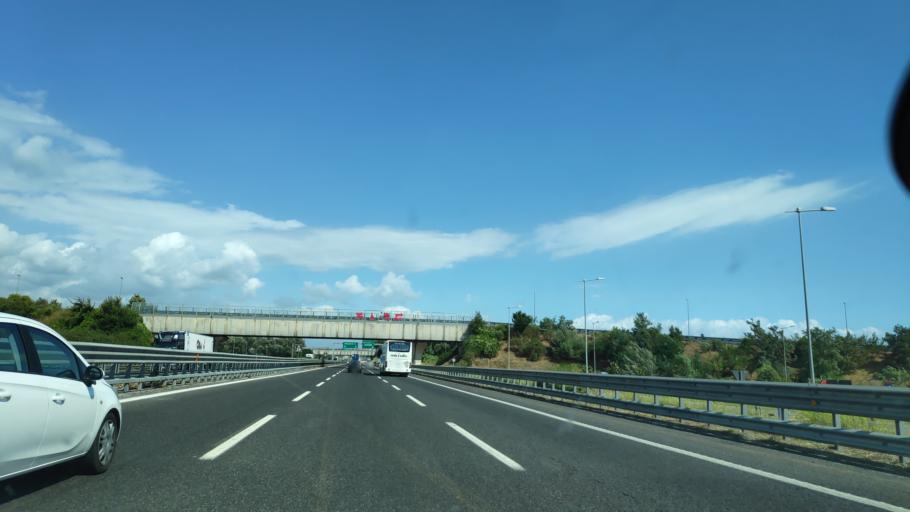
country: IT
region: Campania
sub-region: Provincia di Salerno
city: Pagliarone
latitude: 40.6367
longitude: 14.9095
